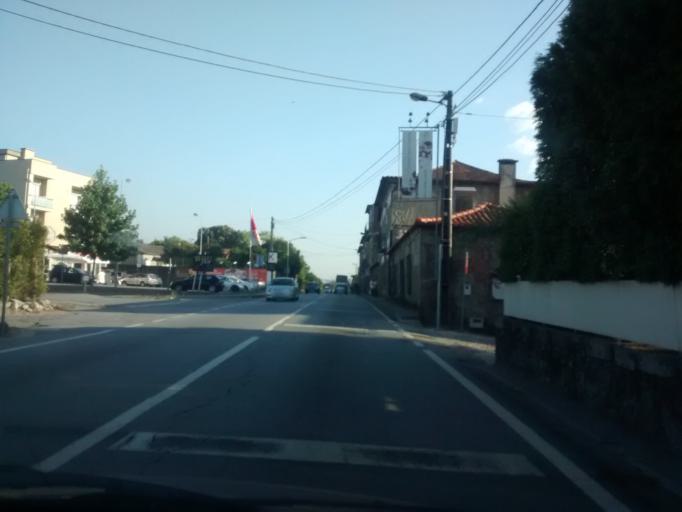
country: PT
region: Braga
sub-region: Braga
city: Adaufe
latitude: 41.5870
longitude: -8.4293
